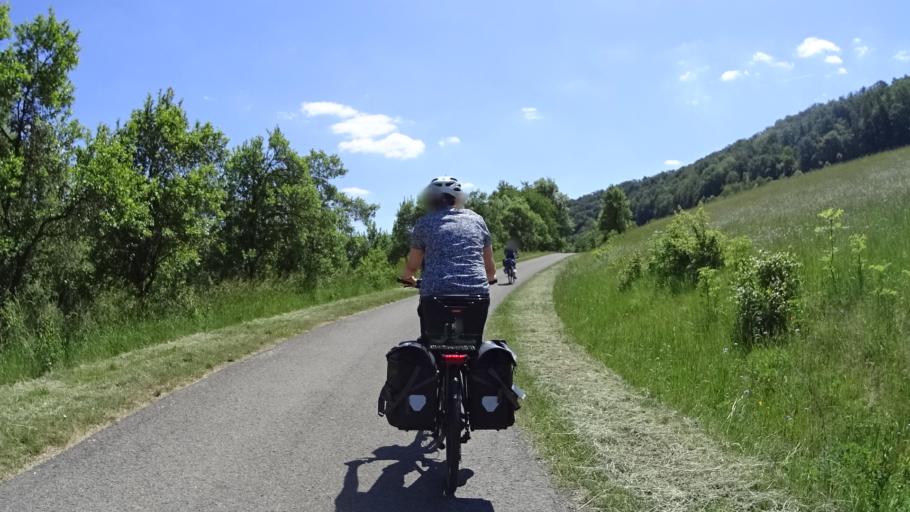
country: DE
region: Bavaria
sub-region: Regierungsbezirk Mittelfranken
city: Adelshofen
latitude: 49.4451
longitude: 10.1227
